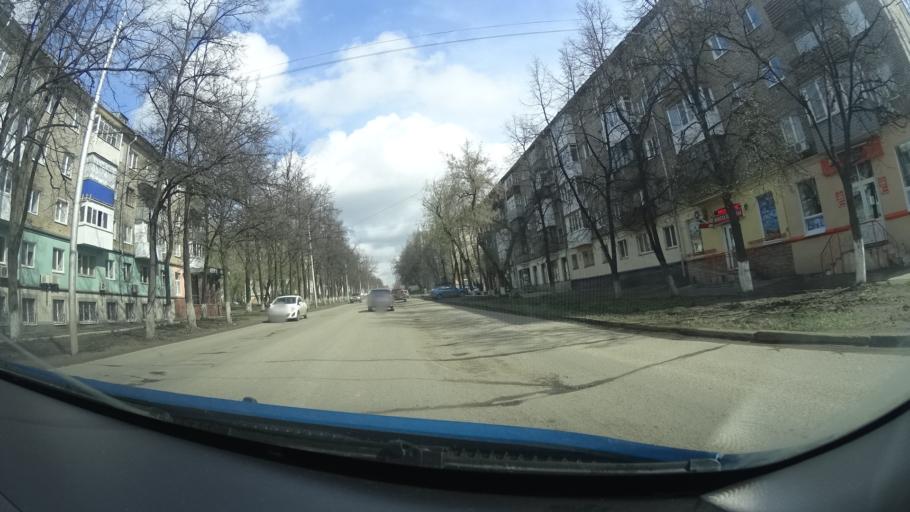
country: RU
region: Bashkortostan
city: Ufa
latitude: 54.8154
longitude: 56.0730
